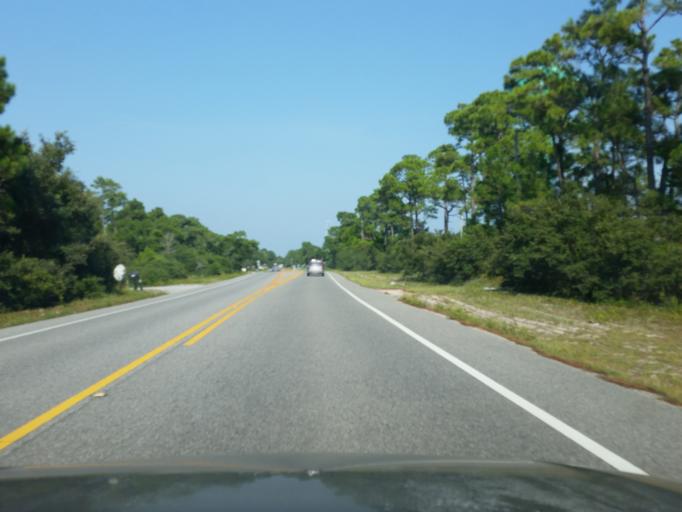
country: US
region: Alabama
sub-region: Baldwin County
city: Gulf Shores
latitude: 30.2379
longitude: -87.8794
